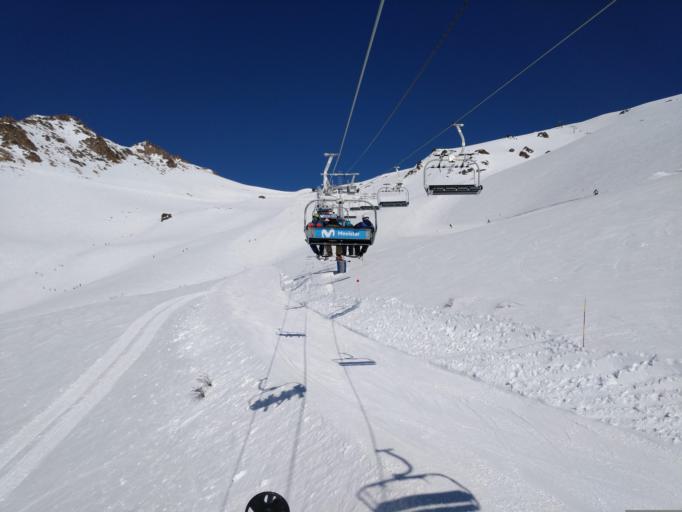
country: AR
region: Rio Negro
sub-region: Departamento de Bariloche
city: San Carlos de Bariloche
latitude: -41.1687
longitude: -71.4745
